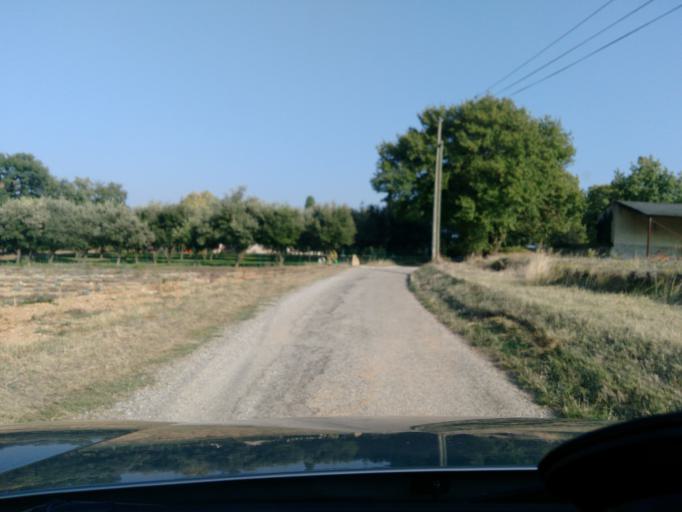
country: FR
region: Rhone-Alpes
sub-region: Departement de la Drome
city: Montboucher-sur-Jabron
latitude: 44.5410
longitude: 4.8359
